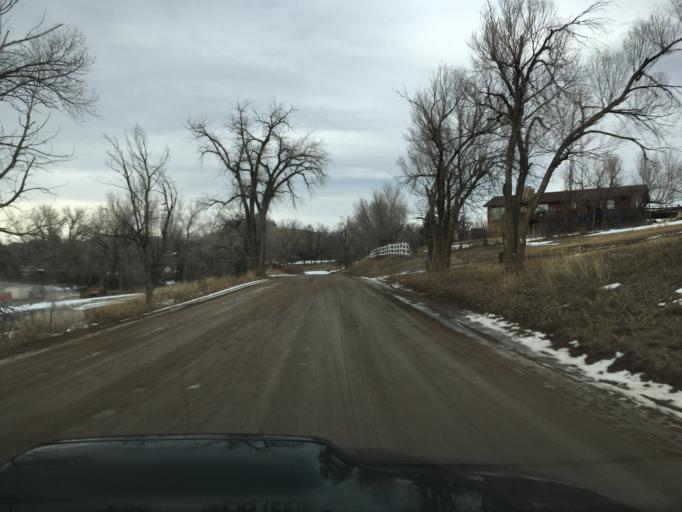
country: US
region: Colorado
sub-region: Larimer County
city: Laporte
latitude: 40.6333
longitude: -105.1493
